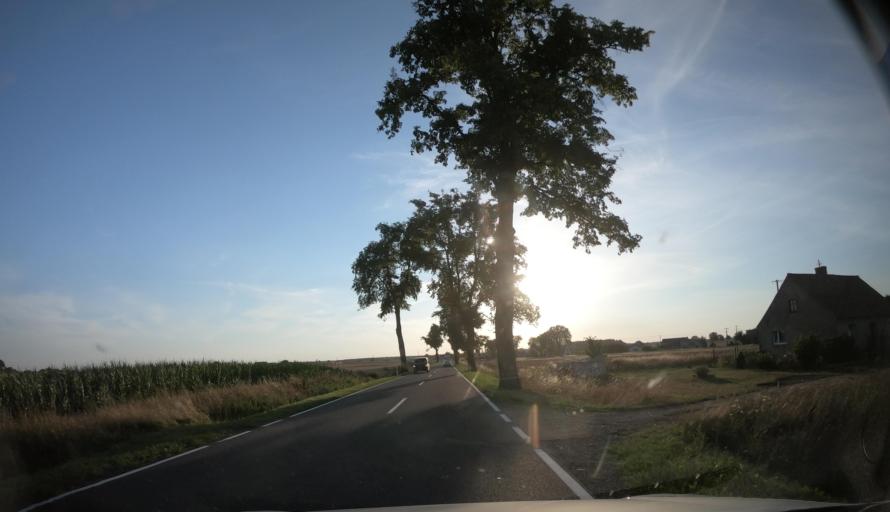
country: PL
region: Kujawsko-Pomorskie
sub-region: Powiat swiecki
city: Pruszcz
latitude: 53.3041
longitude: 18.0922
